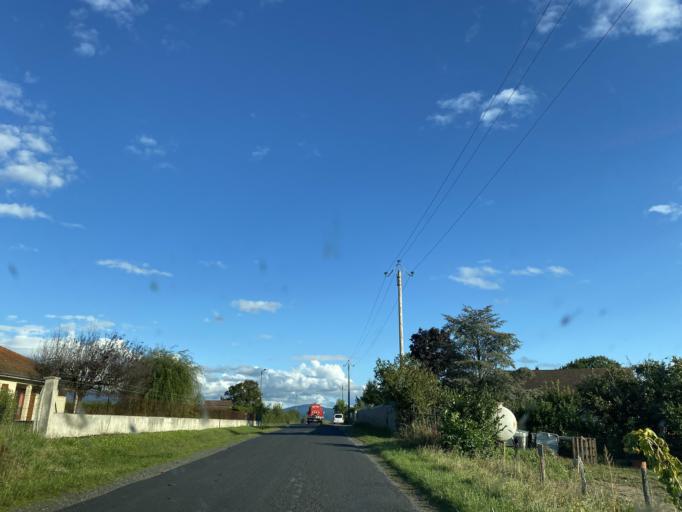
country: FR
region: Auvergne
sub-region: Departement du Puy-de-Dome
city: Saint-Sylvestre-Pragoulin
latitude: 46.0045
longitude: 3.4110
